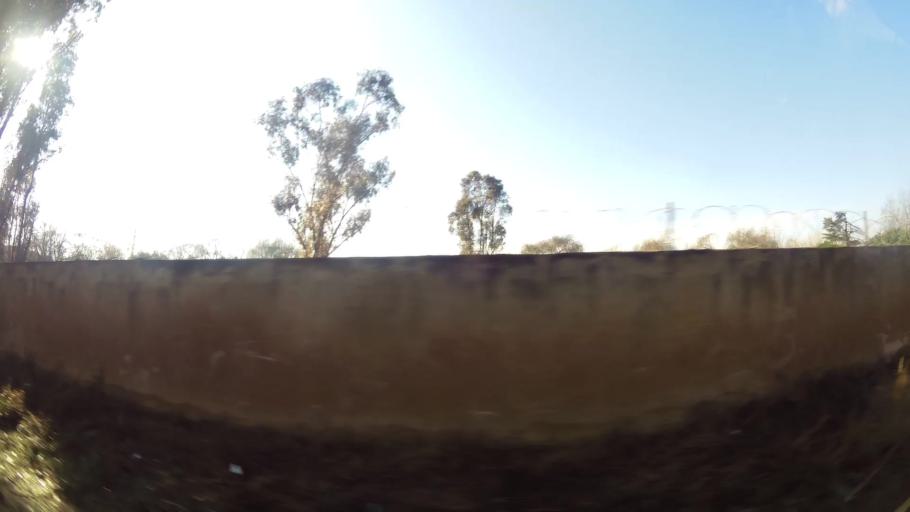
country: ZA
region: Gauteng
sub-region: Sedibeng District Municipality
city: Meyerton
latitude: -26.4960
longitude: 28.0703
